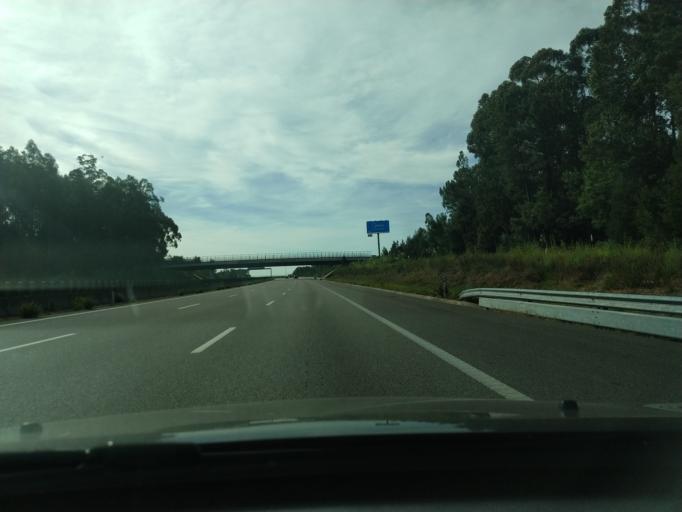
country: PT
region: Aveiro
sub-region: Santa Maria da Feira
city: Feira
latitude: 40.9133
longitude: -8.5680
